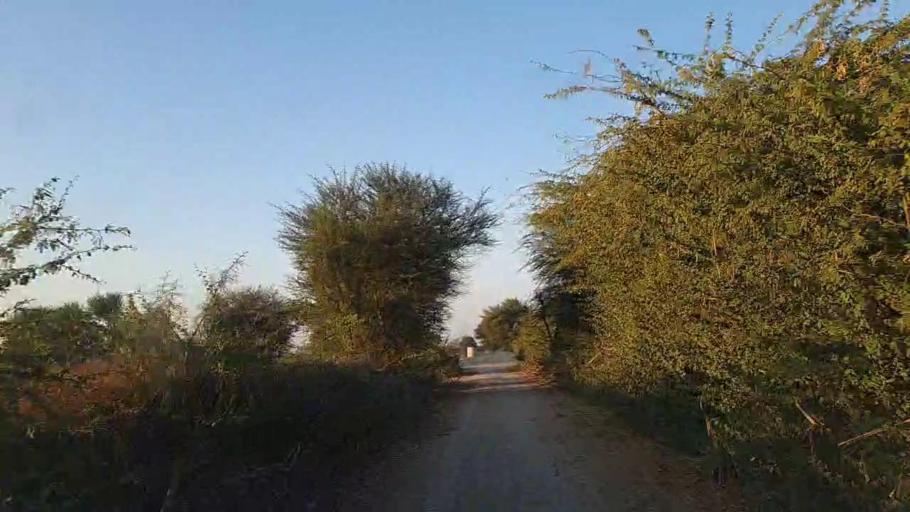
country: PK
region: Sindh
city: Naukot
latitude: 25.0344
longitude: 69.4168
